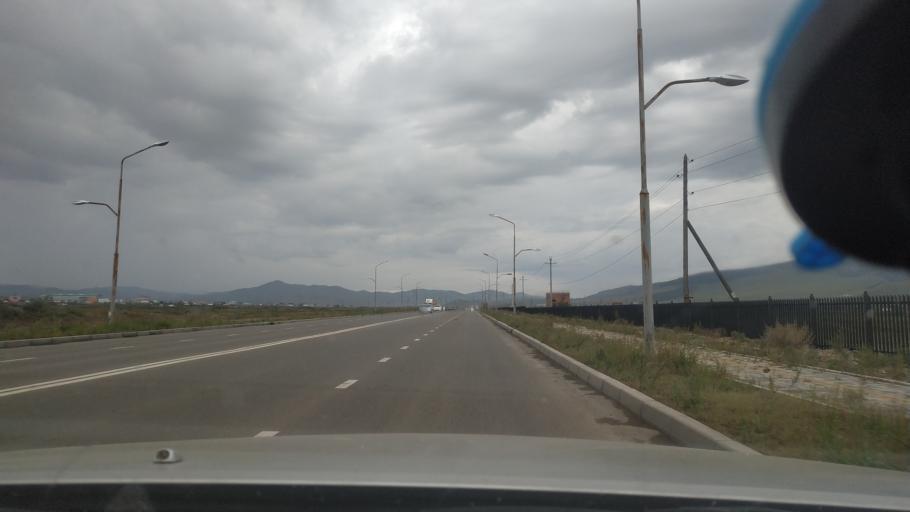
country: MN
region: Ulaanbaatar
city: Ulaanbaatar
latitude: 47.9041
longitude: 106.9769
